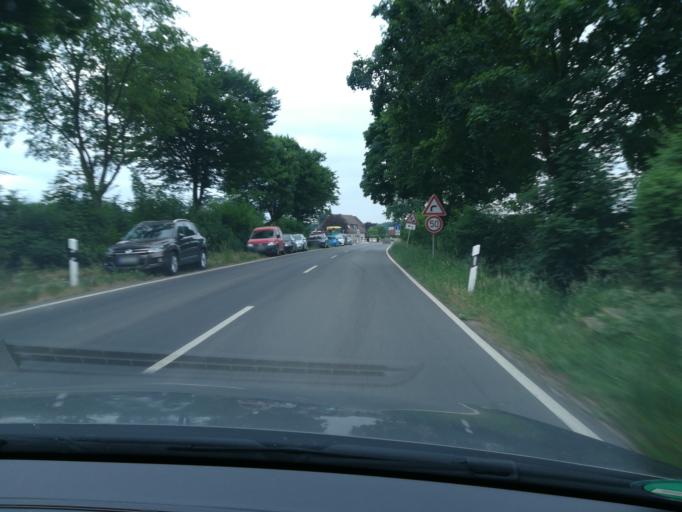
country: DE
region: Schleswig-Holstein
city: Grossensee
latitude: 53.6210
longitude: 10.3362
